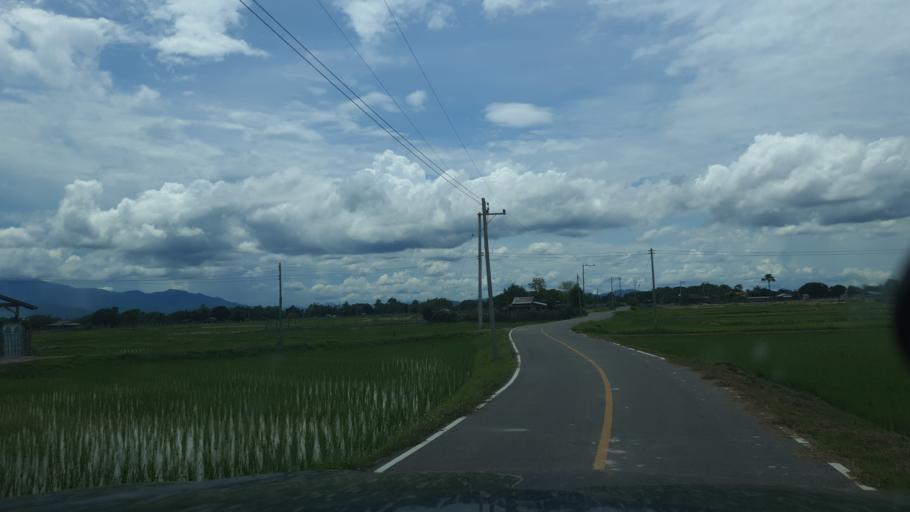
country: TH
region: Lampang
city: Sop Prap
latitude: 17.8727
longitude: 99.3860
